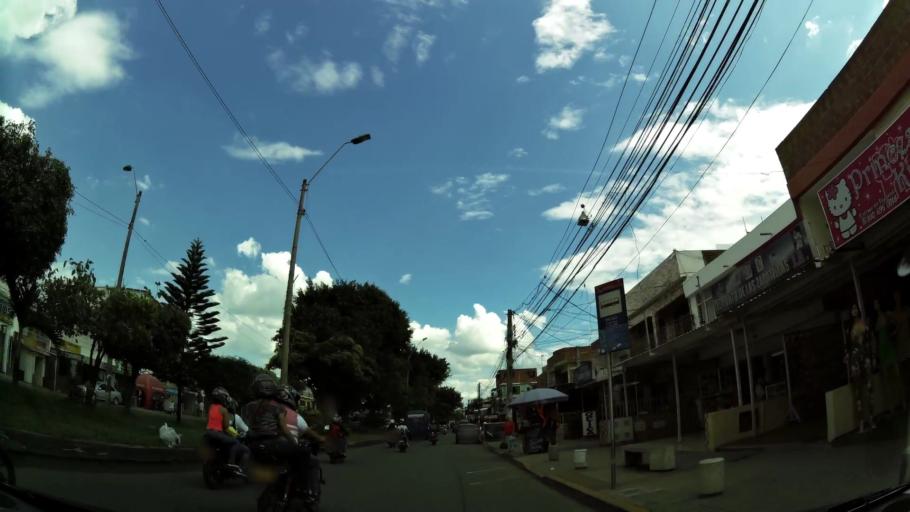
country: CO
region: Valle del Cauca
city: Cali
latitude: 3.4089
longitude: -76.5176
